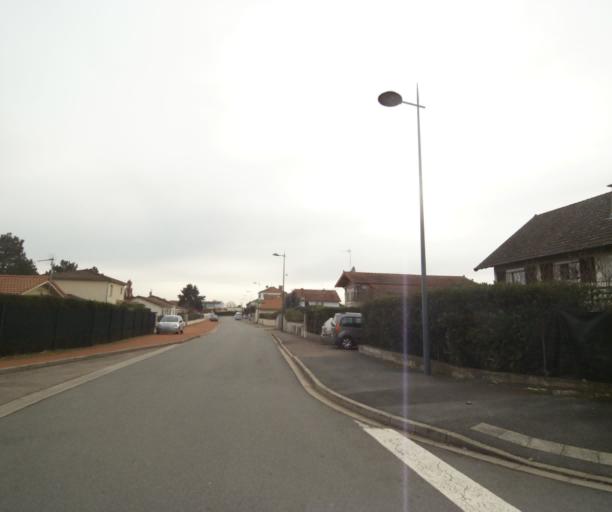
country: FR
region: Rhone-Alpes
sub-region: Departement de la Loire
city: Mably
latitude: 46.0600
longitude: 4.0736
